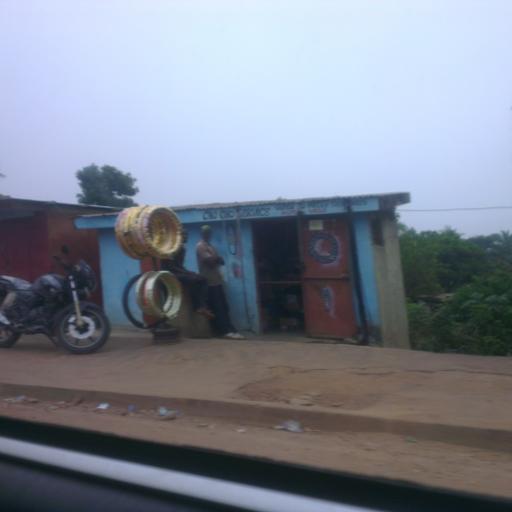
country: CI
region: Vallee du Bandama
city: Bouake
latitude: 7.6824
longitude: -5.0507
